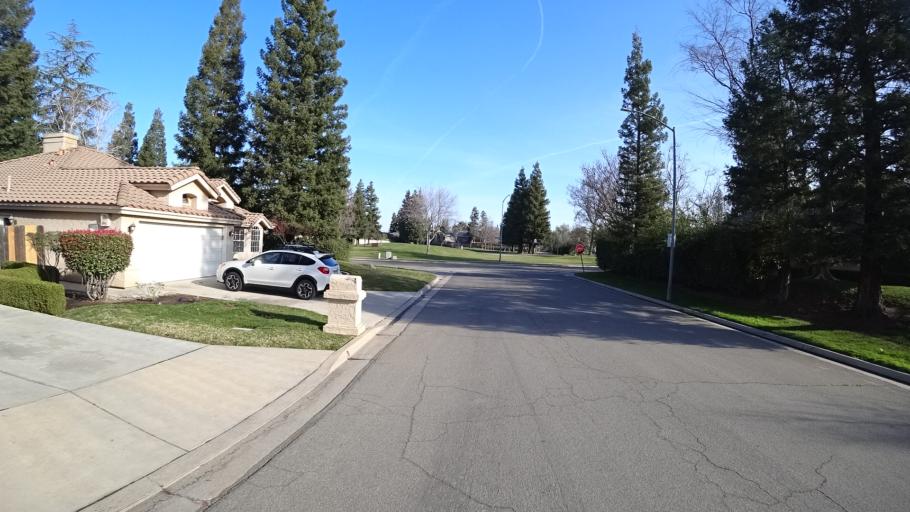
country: US
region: California
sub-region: Fresno County
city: Clovis
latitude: 36.8674
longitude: -119.7640
